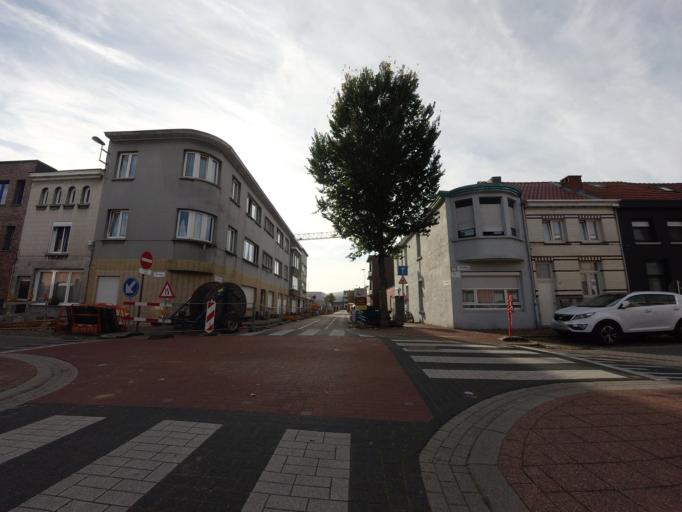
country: BE
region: Flanders
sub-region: Provincie Antwerpen
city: Borsbeek
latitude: 51.2245
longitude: 4.4611
